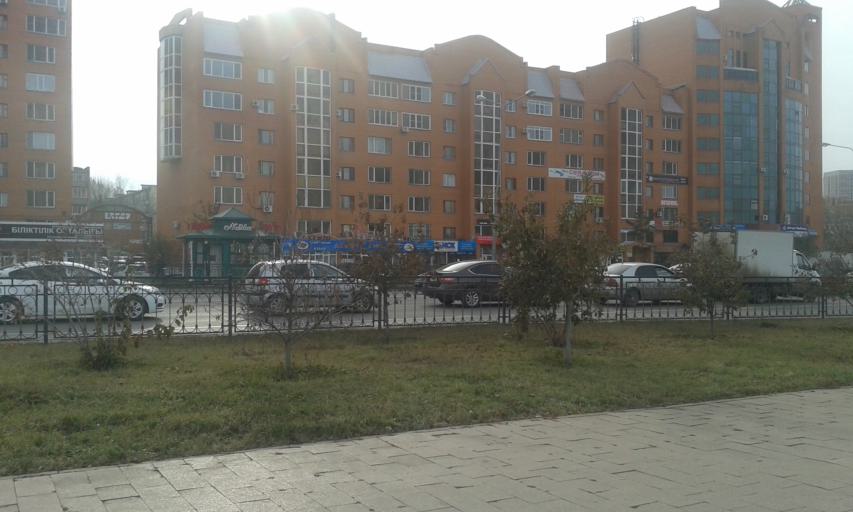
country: KZ
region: Astana Qalasy
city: Astana
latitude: 51.1549
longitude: 71.4685
